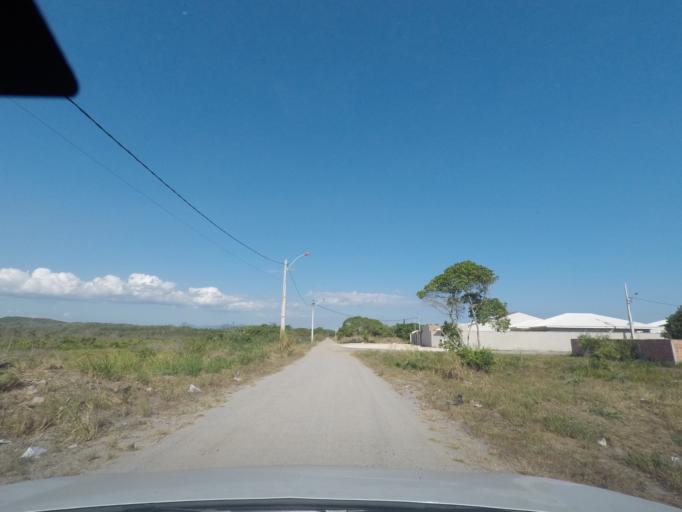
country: BR
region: Rio de Janeiro
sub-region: Marica
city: Marica
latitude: -22.9659
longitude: -42.9177
